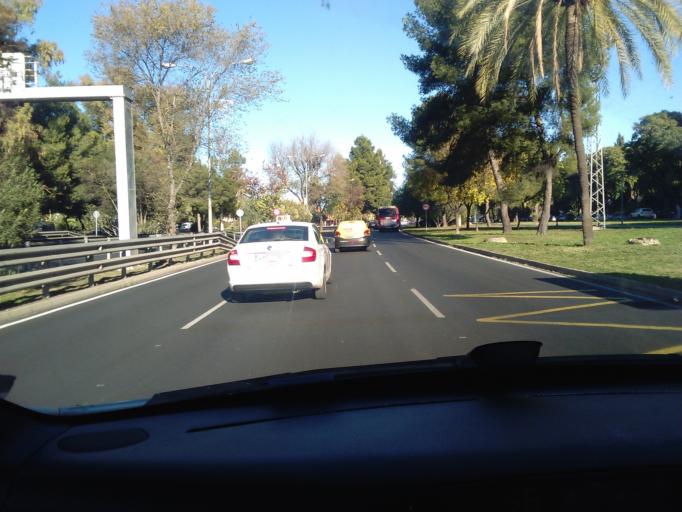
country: ES
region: Andalusia
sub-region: Provincia de Sevilla
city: Sevilla
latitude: 37.4024
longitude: -5.9419
